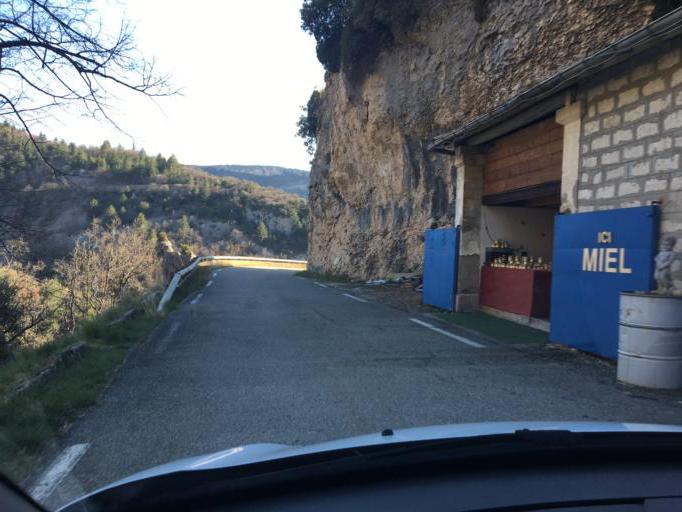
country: FR
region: Provence-Alpes-Cote d'Azur
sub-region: Departement du Vaucluse
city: Villes-sur-Auzon
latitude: 44.0680
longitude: 5.3209
